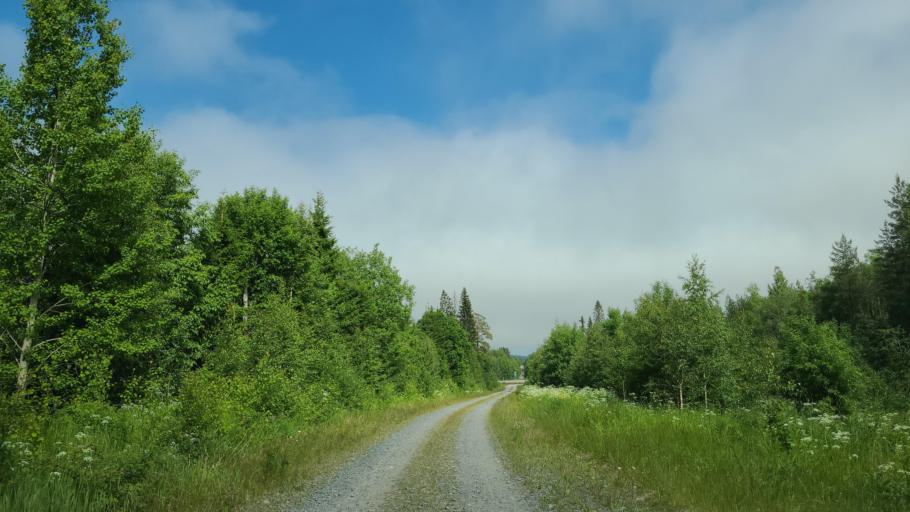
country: SE
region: Vaesternorrland
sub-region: OErnskoeldsviks Kommun
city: Husum
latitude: 63.4540
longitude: 19.2401
